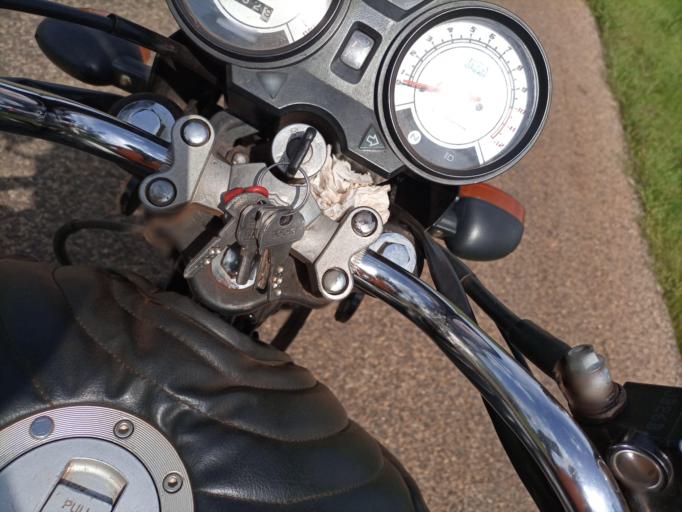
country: GH
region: Northern
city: Savelugu
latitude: 9.5734
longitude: -1.0086
